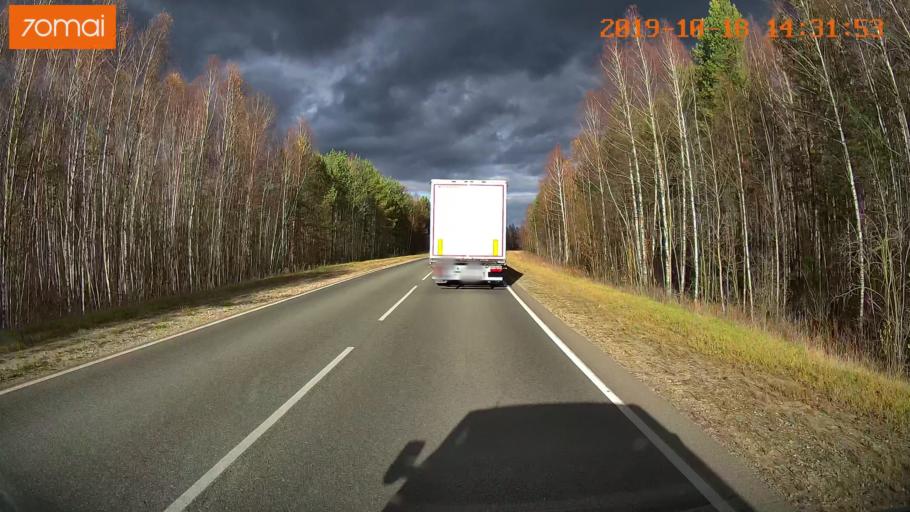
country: RU
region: Rjazan
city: Tuma
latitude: 55.1868
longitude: 40.5731
